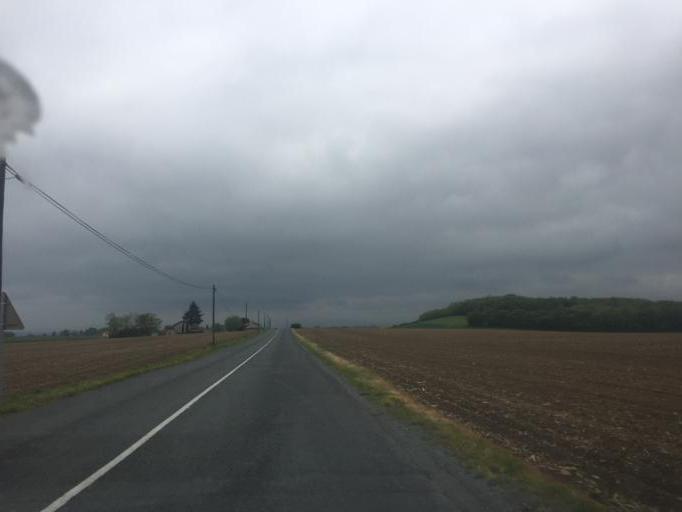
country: FR
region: Rhone-Alpes
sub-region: Departement de l'Ain
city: Civrieux
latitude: 45.9332
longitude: 4.8926
